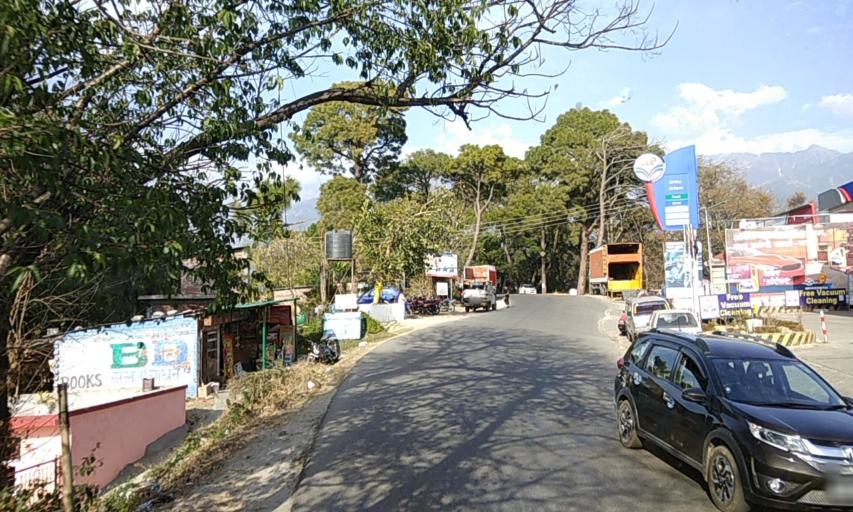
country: IN
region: Himachal Pradesh
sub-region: Kangra
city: Palampur
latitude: 32.0964
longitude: 76.5306
